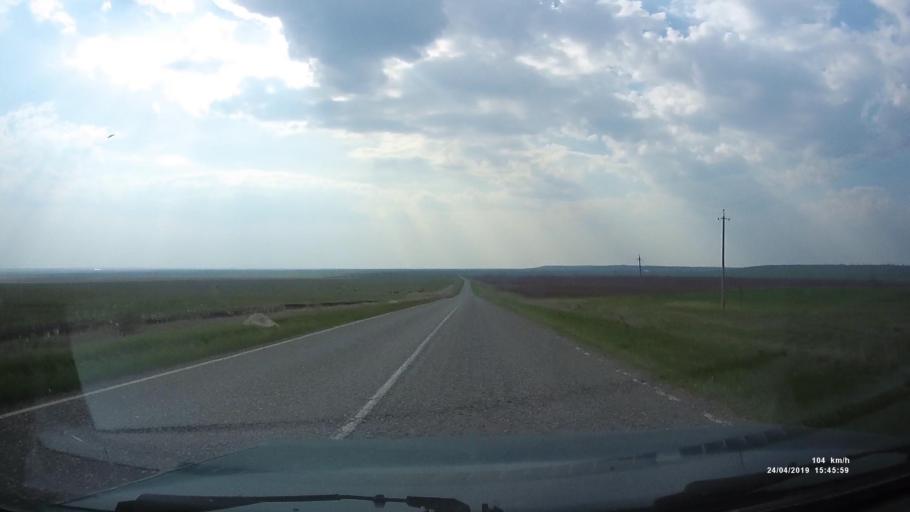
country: RU
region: Kalmykiya
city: Yashalta
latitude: 46.5921
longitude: 42.7251
